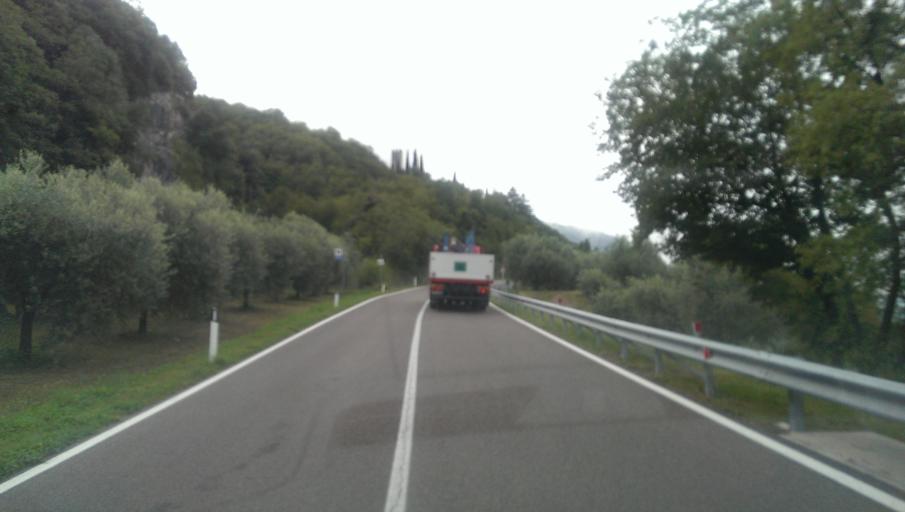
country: IT
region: Trentino-Alto Adige
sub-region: Provincia di Trento
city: Drena
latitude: 45.9737
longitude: 10.9394
